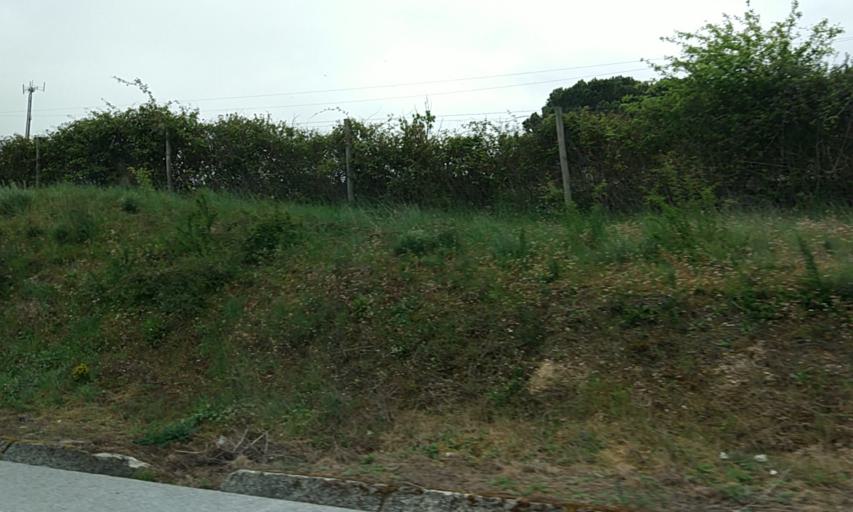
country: PT
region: Guarda
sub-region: Celorico da Beira
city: Celorico da Beira
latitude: 40.6268
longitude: -7.3785
